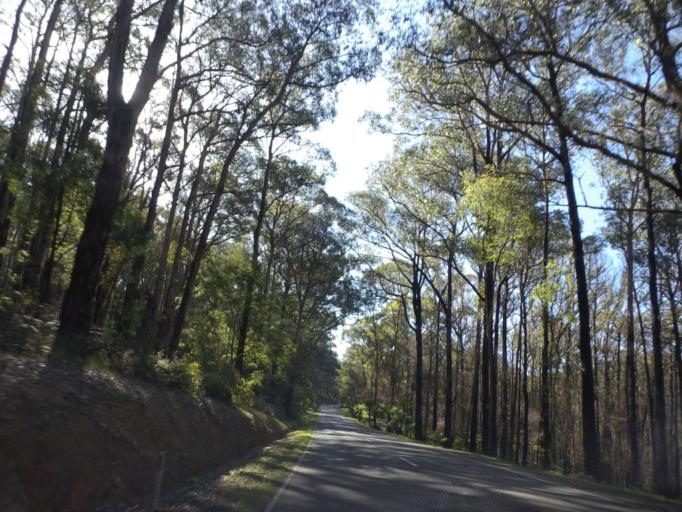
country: AU
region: Victoria
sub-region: Yarra Ranges
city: Yarra Junction
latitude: -37.8371
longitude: 145.6768
